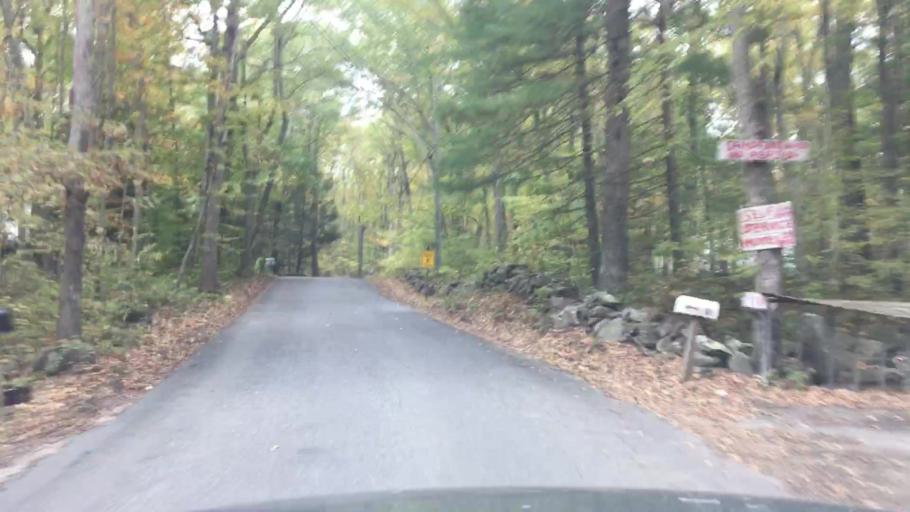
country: US
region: Connecticut
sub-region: Tolland County
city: Storrs
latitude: 41.8802
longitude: -72.1718
